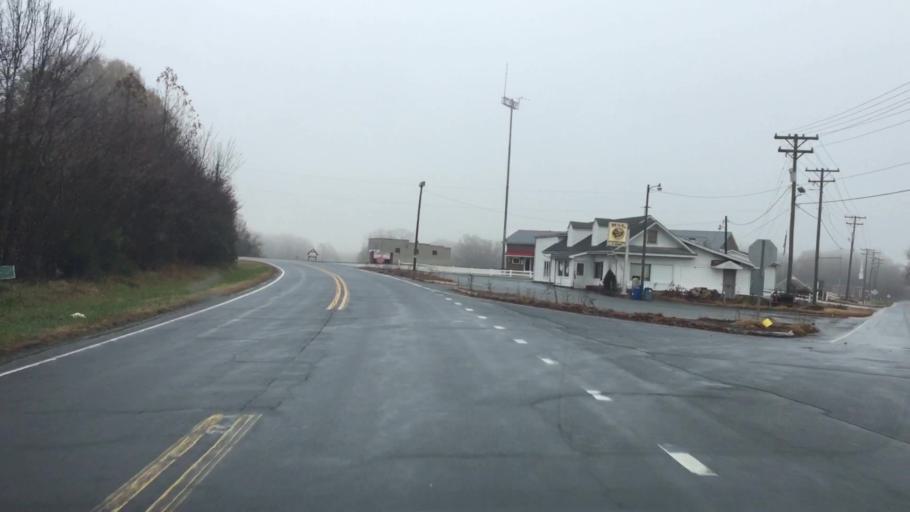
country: US
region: North Carolina
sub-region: Rockingham County
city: Reidsville
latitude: 36.2901
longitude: -79.7321
